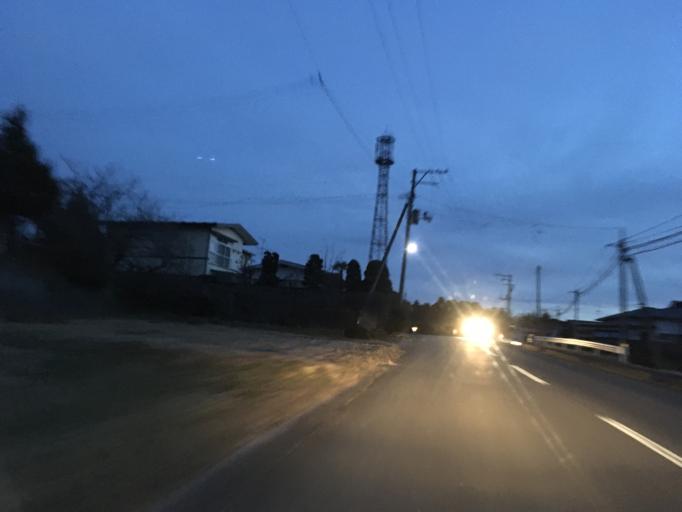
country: JP
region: Miyagi
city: Wakuya
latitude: 38.6949
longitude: 141.1644
